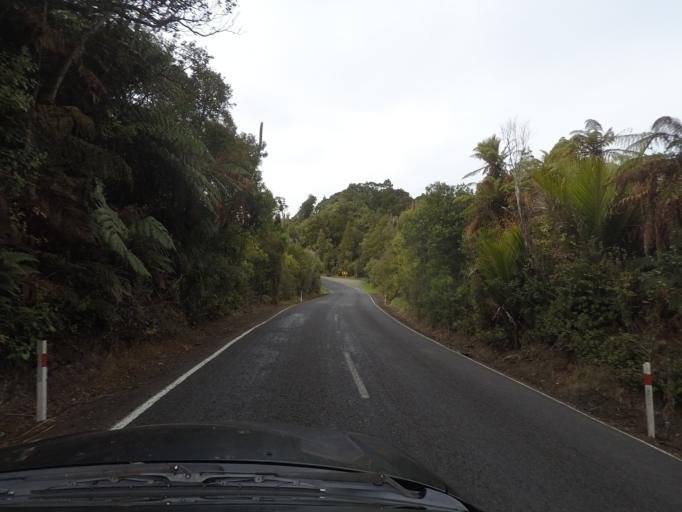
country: NZ
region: Auckland
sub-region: Auckland
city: Titirangi
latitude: -36.9424
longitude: 174.5926
